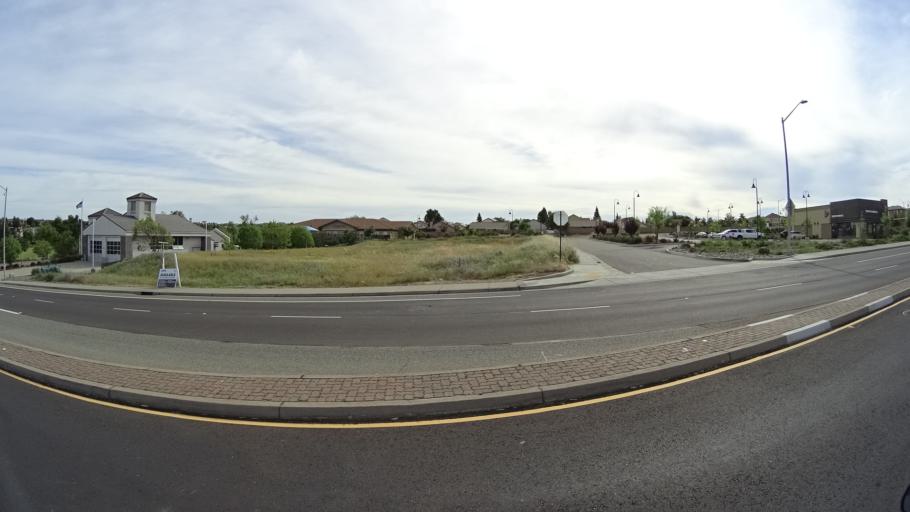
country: US
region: California
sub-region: Placer County
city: Rocklin
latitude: 38.8192
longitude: -121.2814
